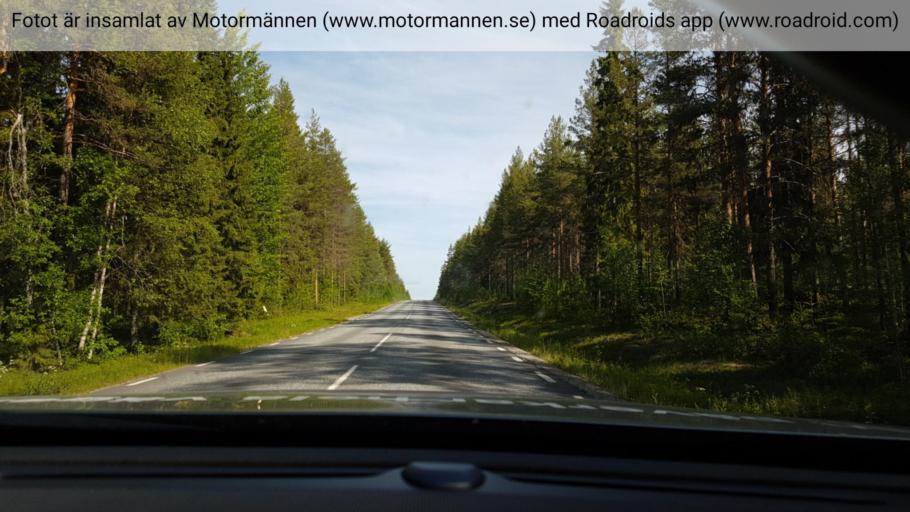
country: SE
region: Vaesterbotten
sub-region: Dorotea Kommun
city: Dorotea
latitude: 64.2701
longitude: 16.3468
